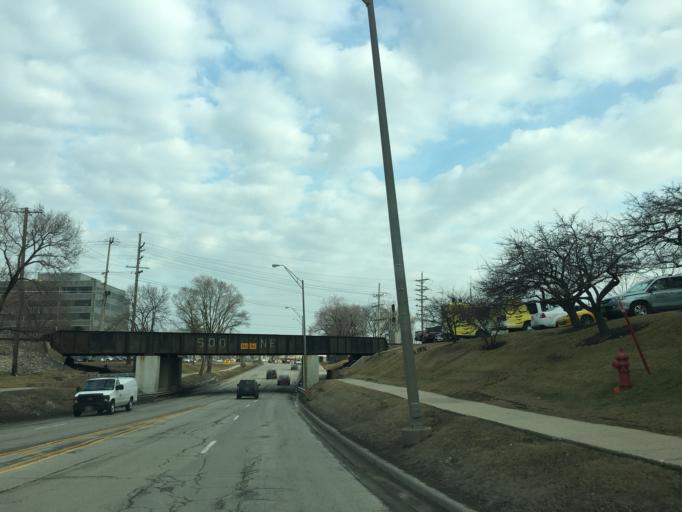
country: US
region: Illinois
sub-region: Cook County
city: Rosemont
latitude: 41.9976
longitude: -87.8821
